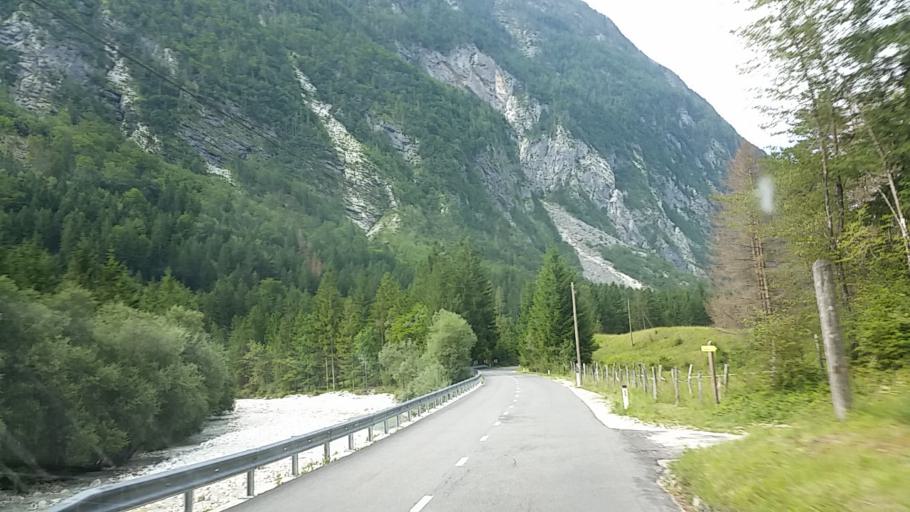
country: SI
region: Kranjska Gora
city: Kranjska Gora
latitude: 46.3697
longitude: 13.7268
